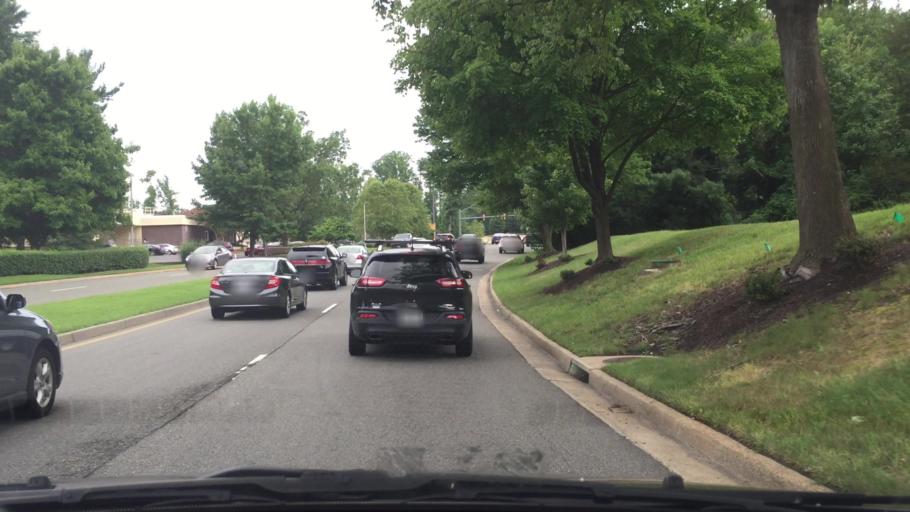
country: US
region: Virginia
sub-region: Henrico County
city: Tuckahoe
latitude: 37.6047
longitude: -77.5274
